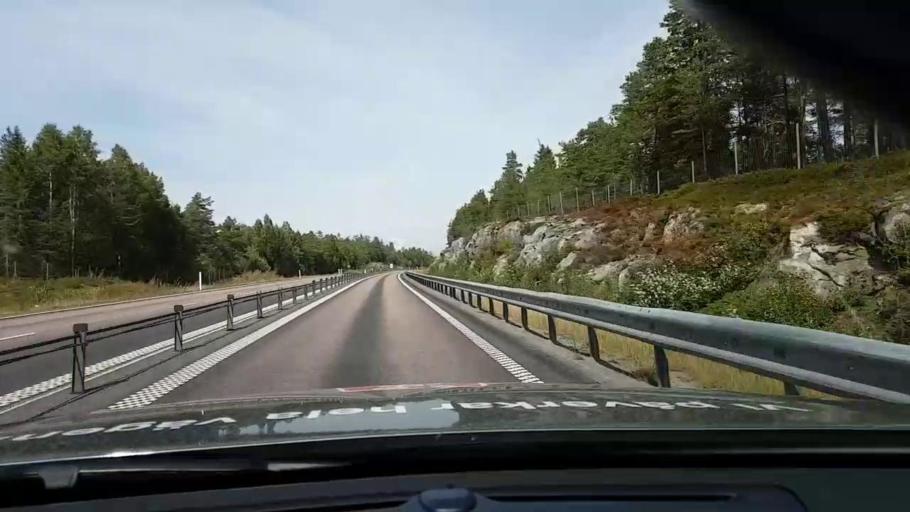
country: SE
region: Vaesternorrland
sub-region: OErnskoeldsviks Kommun
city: Husum
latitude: 63.3776
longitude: 19.1907
